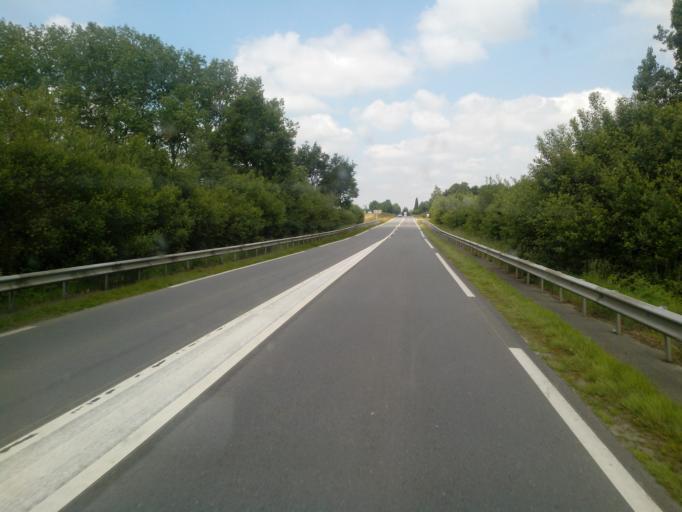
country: FR
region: Brittany
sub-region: Departement d'Ille-et-Vilaine
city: Saint-Germain-en-Cogles
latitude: 48.3874
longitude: -1.2764
